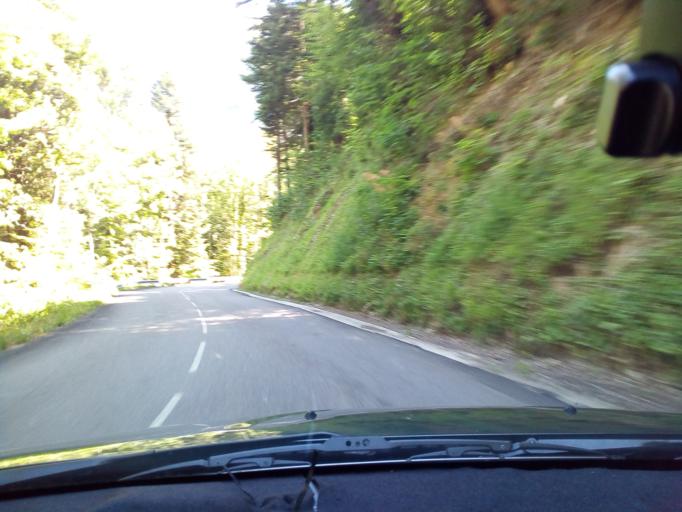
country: FR
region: Rhone-Alpes
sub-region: Departement de l'Isere
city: Meaudre
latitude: 45.0799
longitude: 5.4830
